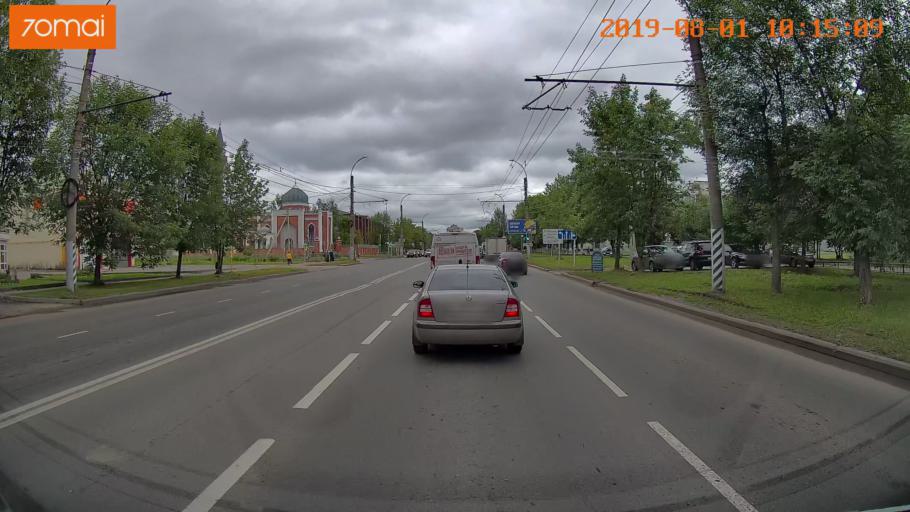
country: RU
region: Ivanovo
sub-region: Gorod Ivanovo
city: Ivanovo
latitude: 56.9640
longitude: 40.9829
